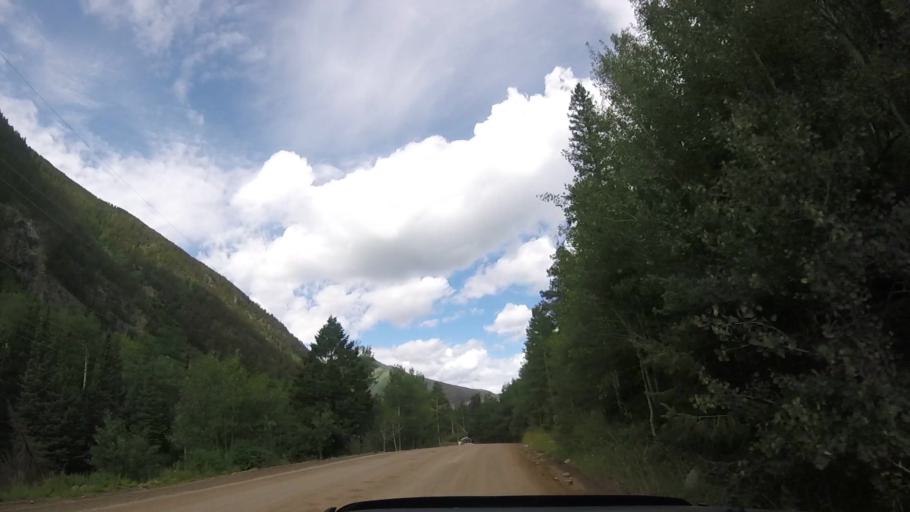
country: US
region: Colorado
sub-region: San Miguel County
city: Mountain Village
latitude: 37.8587
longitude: -107.8635
